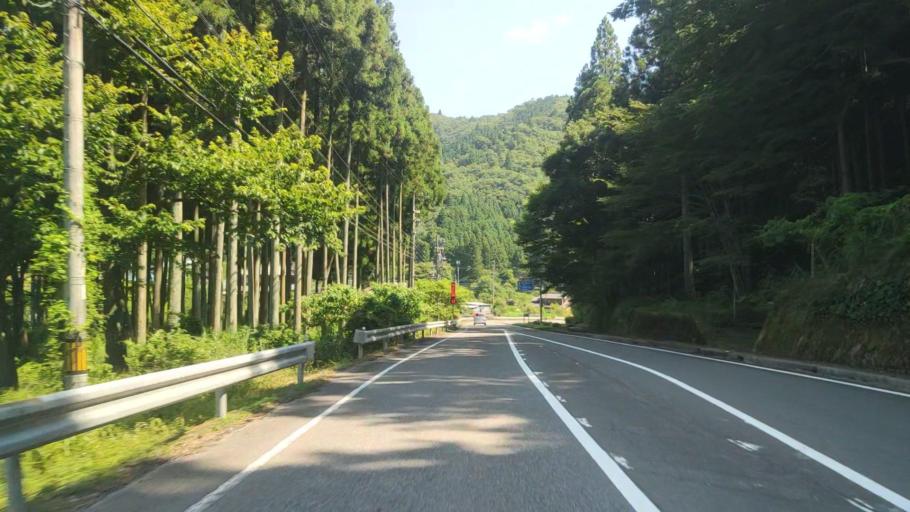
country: JP
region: Gifu
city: Godo
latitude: 35.5652
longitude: 136.6486
